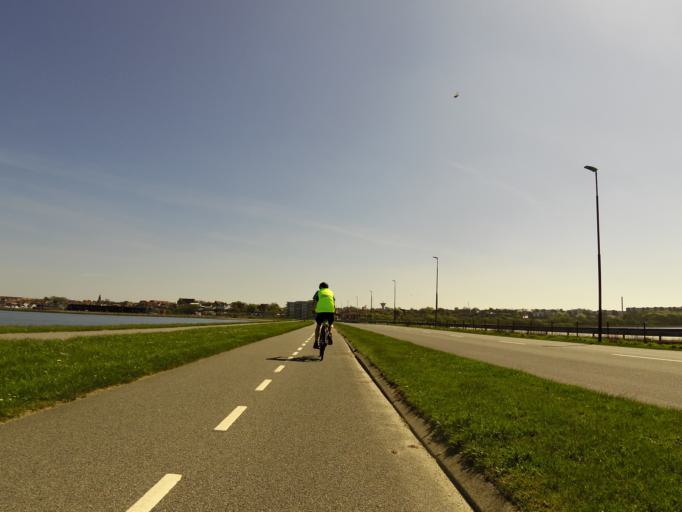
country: DK
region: Central Jutland
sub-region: Struer Kommune
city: Struer
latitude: 56.4994
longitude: 8.5826
